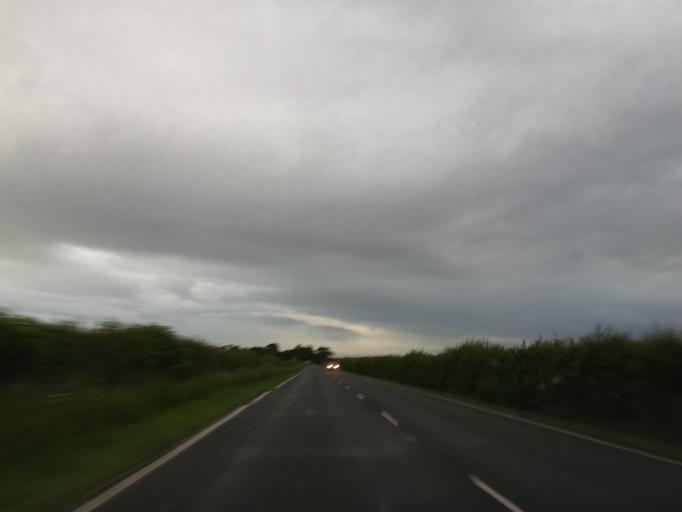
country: GB
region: Scotland
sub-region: East Lothian
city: Dunbar
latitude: 55.9935
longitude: -2.5647
